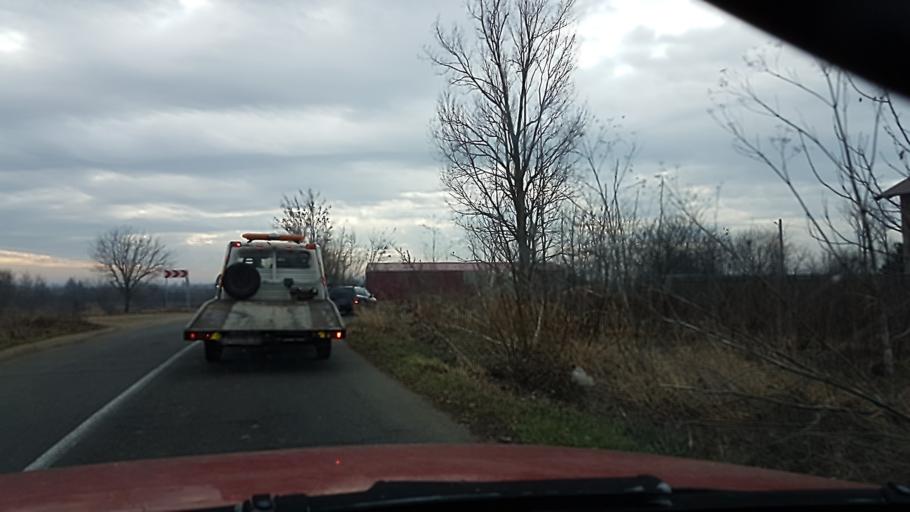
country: RO
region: Giurgiu
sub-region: Comuna Herasti
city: Herasti
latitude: 44.2204
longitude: 26.3614
